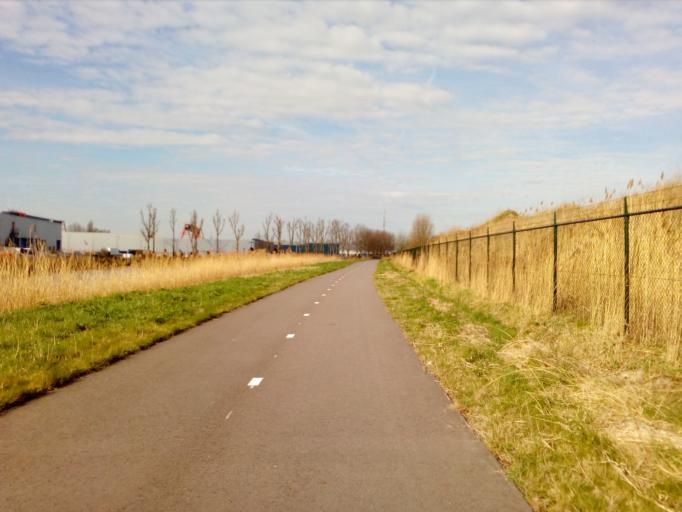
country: NL
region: South Holland
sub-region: Gemeente Schiedam
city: Schiedam
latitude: 51.9463
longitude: 4.4040
